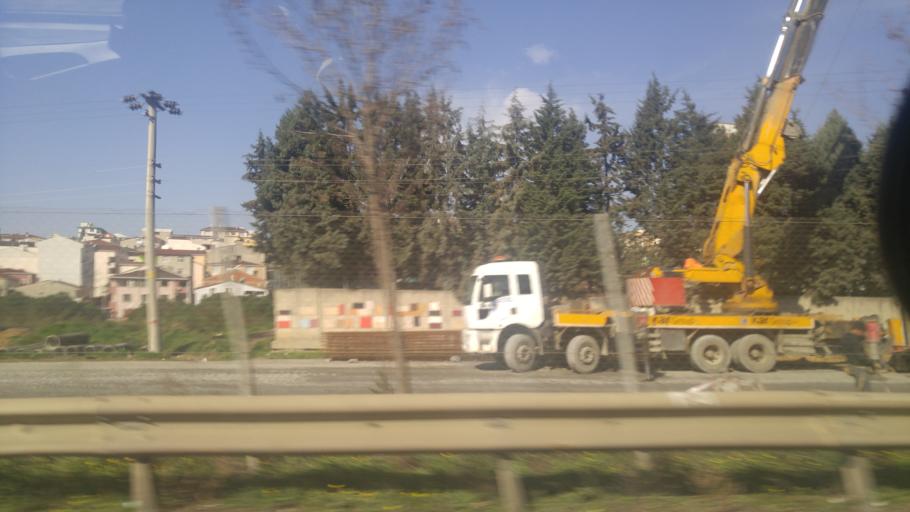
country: TR
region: Kocaeli
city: Darica
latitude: 40.8297
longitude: 29.3670
